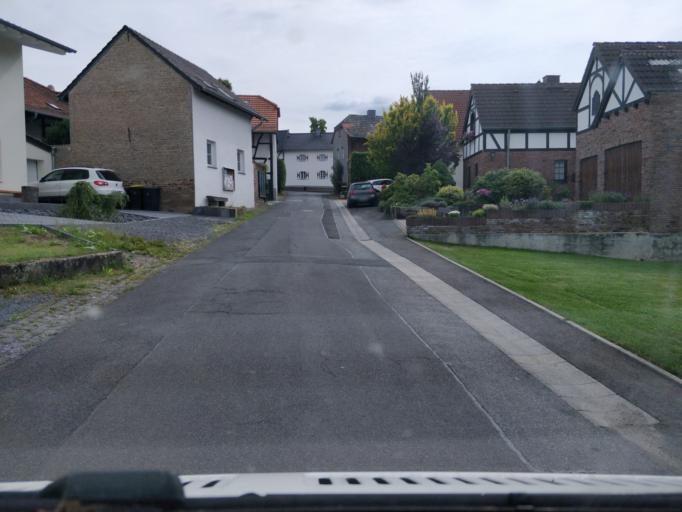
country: DE
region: North Rhine-Westphalia
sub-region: Regierungsbezirk Koln
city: Rheinbach
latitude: 50.6031
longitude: 6.9260
